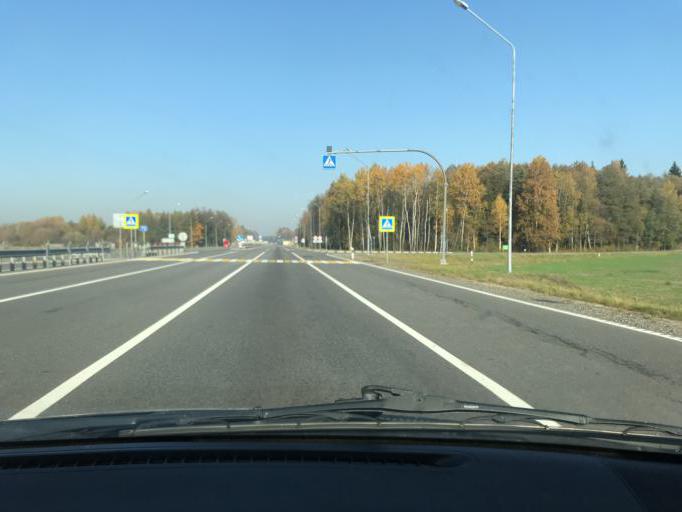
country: BY
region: Minsk
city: Slutsk
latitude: 53.2713
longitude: 27.5502
